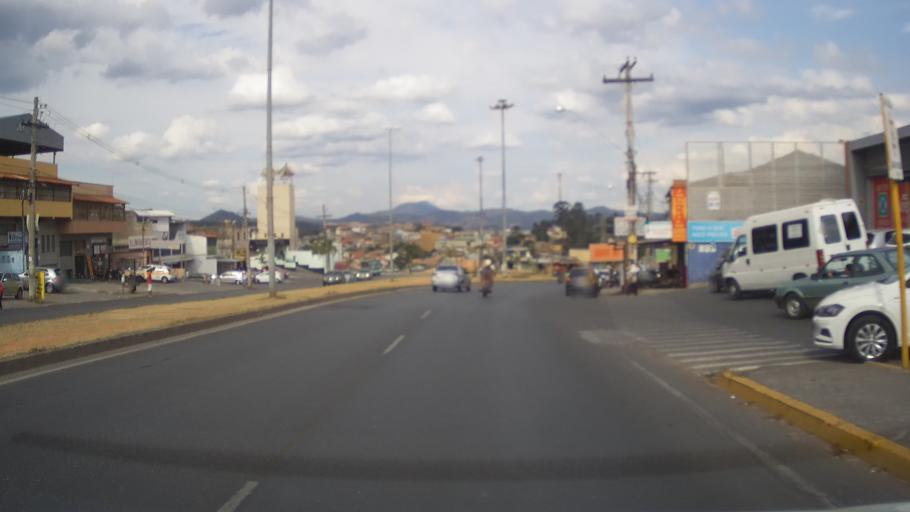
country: BR
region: Minas Gerais
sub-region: Belo Horizonte
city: Belo Horizonte
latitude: -19.8757
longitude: -43.9058
